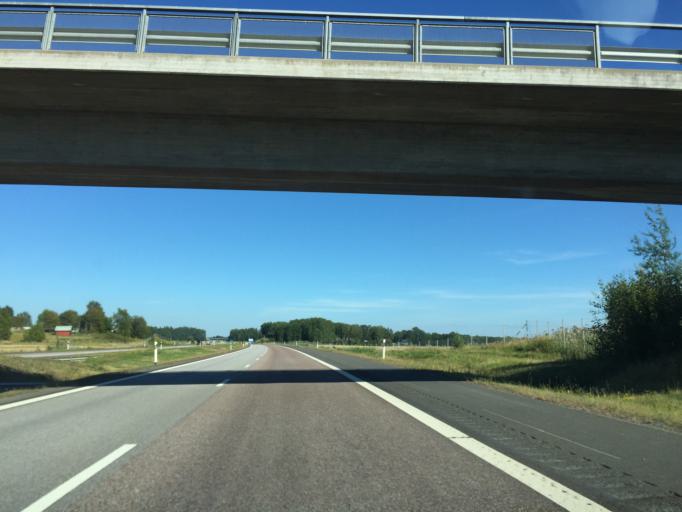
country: SE
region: OErebro
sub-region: Orebro Kommun
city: Hovsta
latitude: 59.3064
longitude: 15.3694
